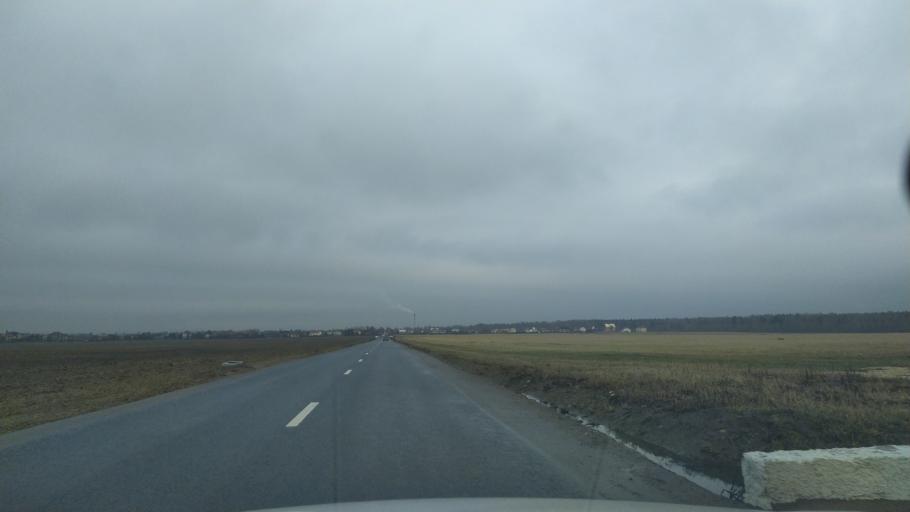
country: RU
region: St.-Petersburg
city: Aleksandrovskaya
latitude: 59.7147
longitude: 30.3349
